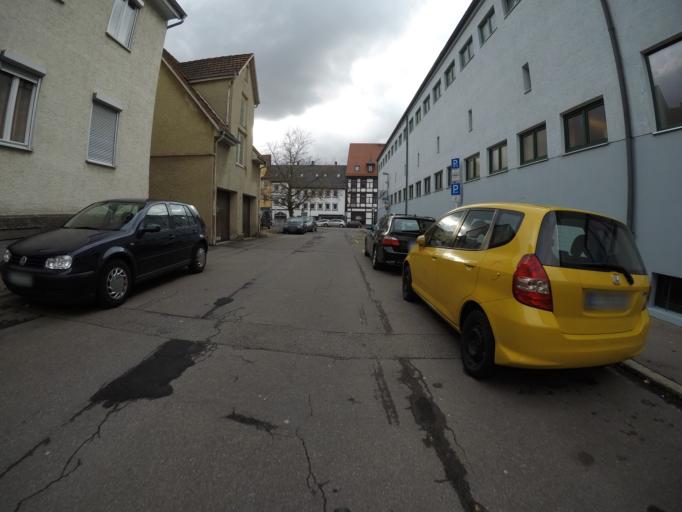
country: DE
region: Baden-Wuerttemberg
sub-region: Tuebingen Region
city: Reutlingen
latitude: 48.4893
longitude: 9.2185
